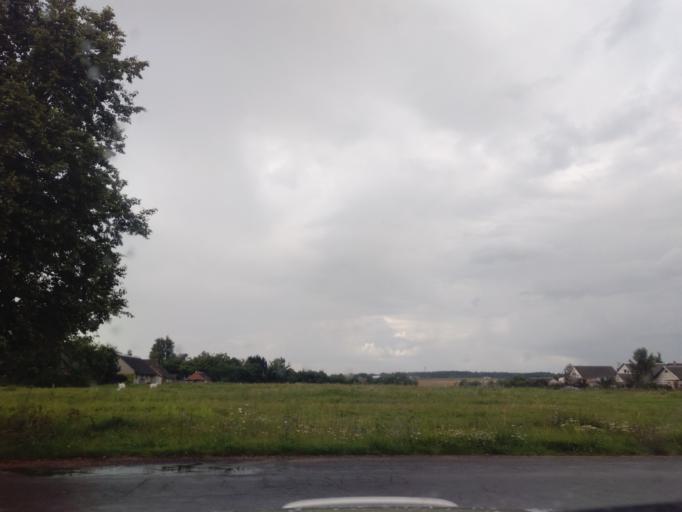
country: BY
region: Minsk
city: Kapyl'
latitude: 53.1655
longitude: 27.0850
